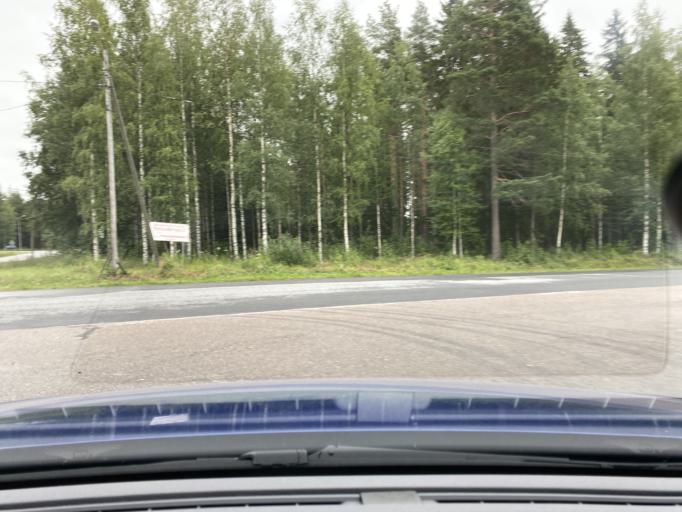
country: FI
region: Pirkanmaa
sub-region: Ylae-Pirkanmaa
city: Vilppula
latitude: 62.2422
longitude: 24.4628
